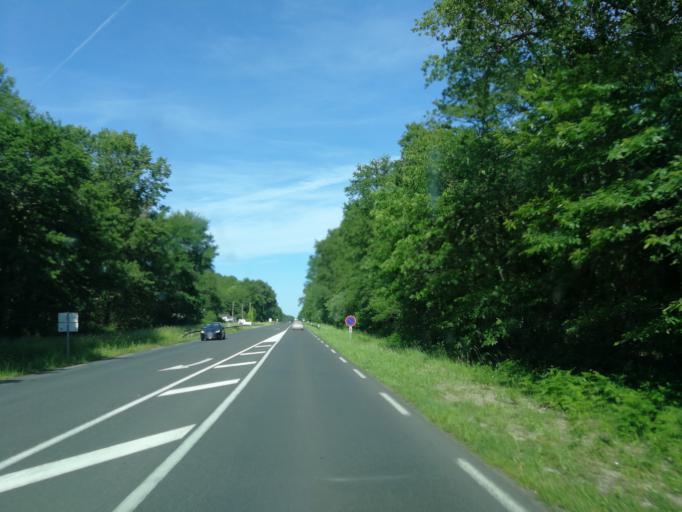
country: FR
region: Centre
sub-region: Departement d'Indre-et-Loire
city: Huismes
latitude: 47.2050
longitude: 0.3324
